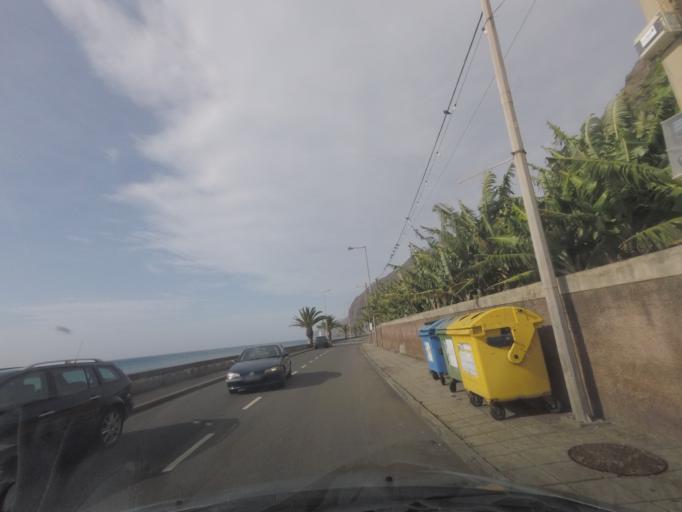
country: PT
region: Madeira
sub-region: Calheta
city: Arco da Calheta
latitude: 32.6934
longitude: -17.1255
